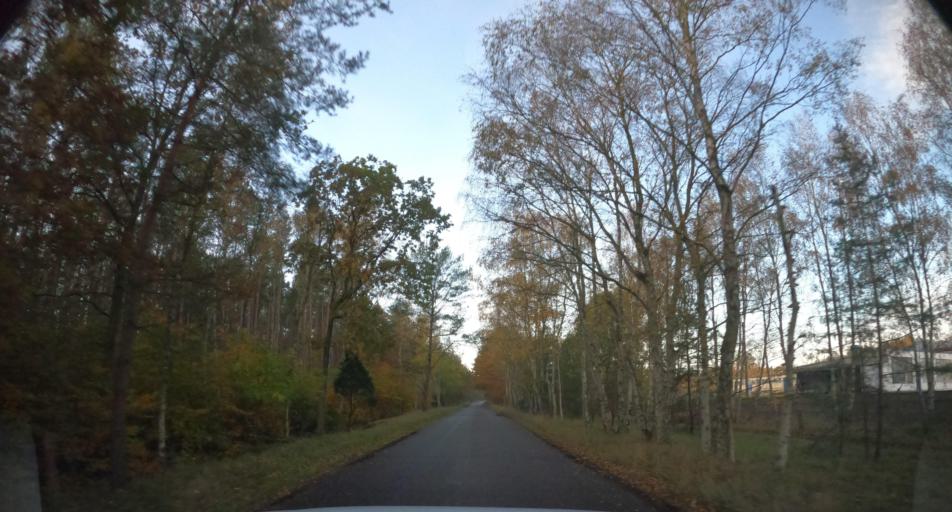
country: PL
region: West Pomeranian Voivodeship
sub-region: Powiat policki
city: Police
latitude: 53.6489
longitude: 14.4502
